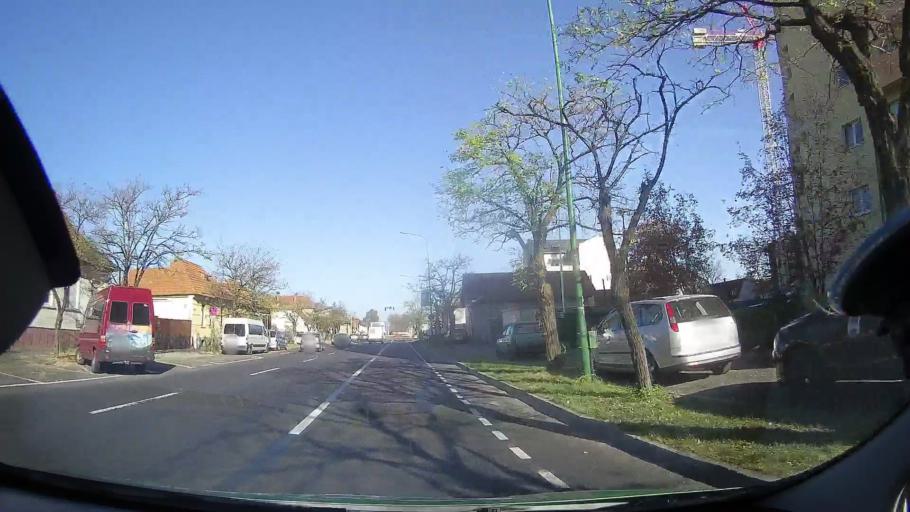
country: RO
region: Brasov
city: Brasov
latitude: 45.6632
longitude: 25.5813
